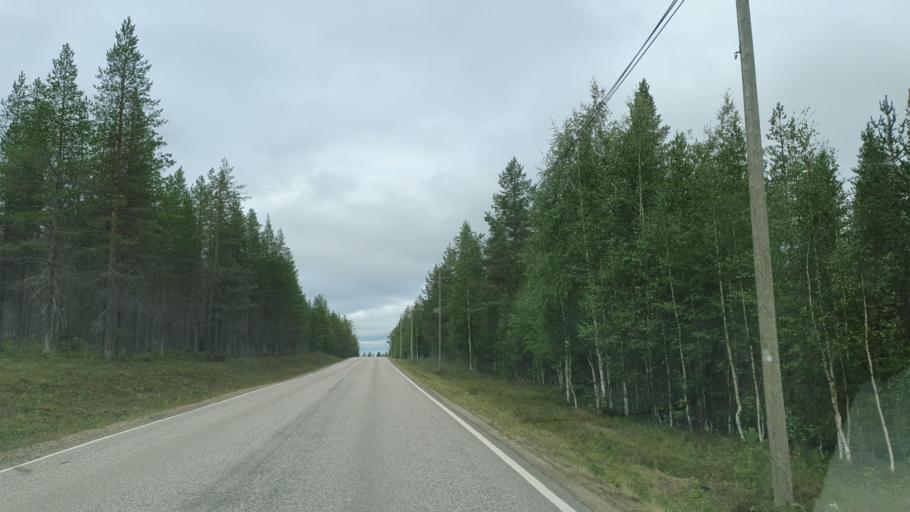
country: FI
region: Lapland
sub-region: Pohjois-Lappi
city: Sodankylae
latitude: 67.4161
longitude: 26.2903
